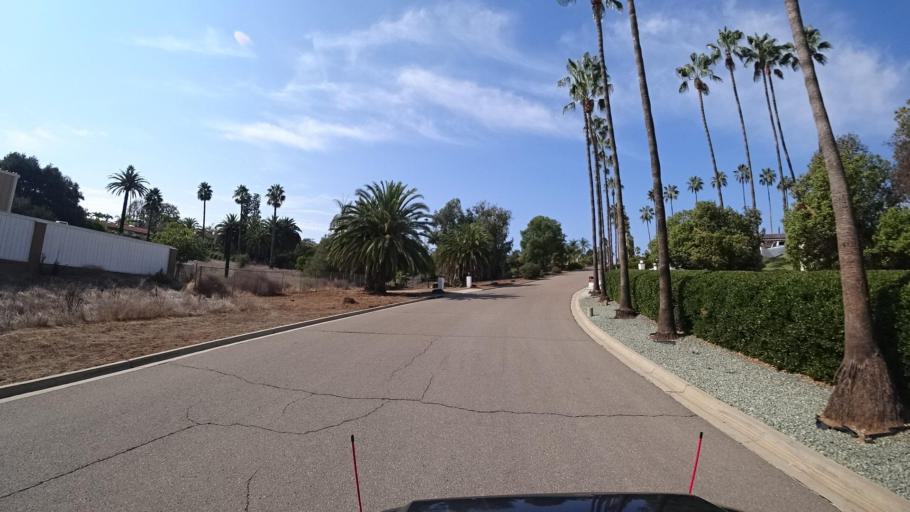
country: US
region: California
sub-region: San Diego County
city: Escondido
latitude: 33.0888
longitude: -117.0595
